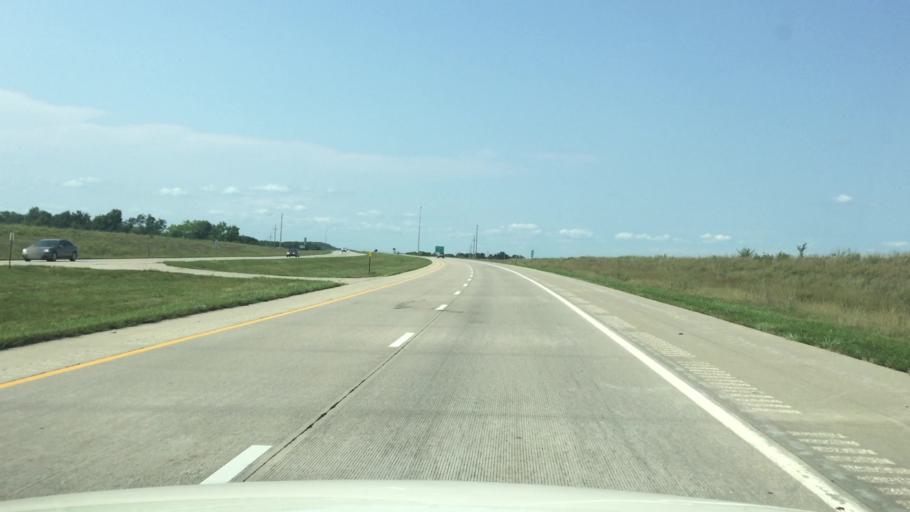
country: US
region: Kansas
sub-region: Linn County
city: Pleasanton
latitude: 38.1745
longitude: -94.6962
